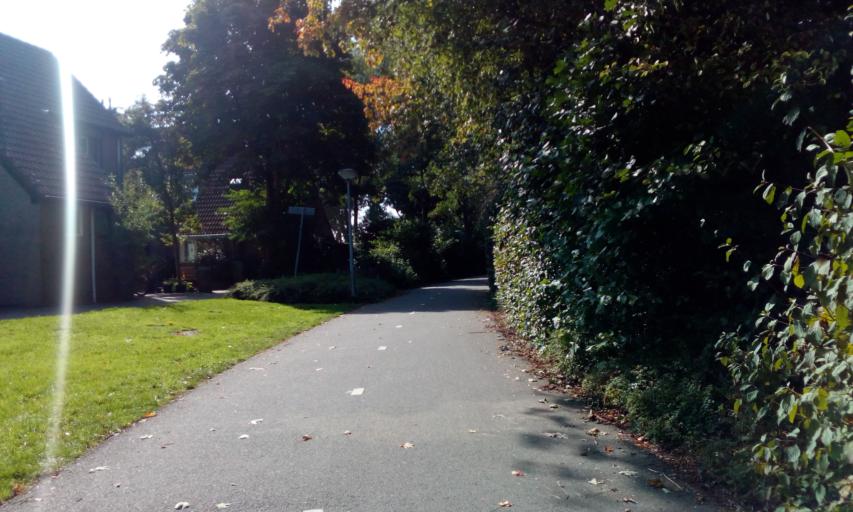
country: NL
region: South Holland
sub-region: Gemeente Voorschoten
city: Voorschoten
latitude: 52.1414
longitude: 4.4558
